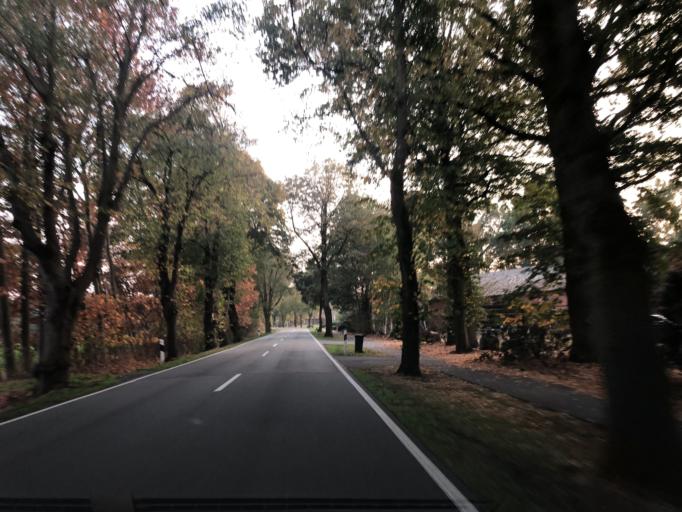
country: DE
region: Lower Saxony
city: Garrel
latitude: 53.0089
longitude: 8.0416
